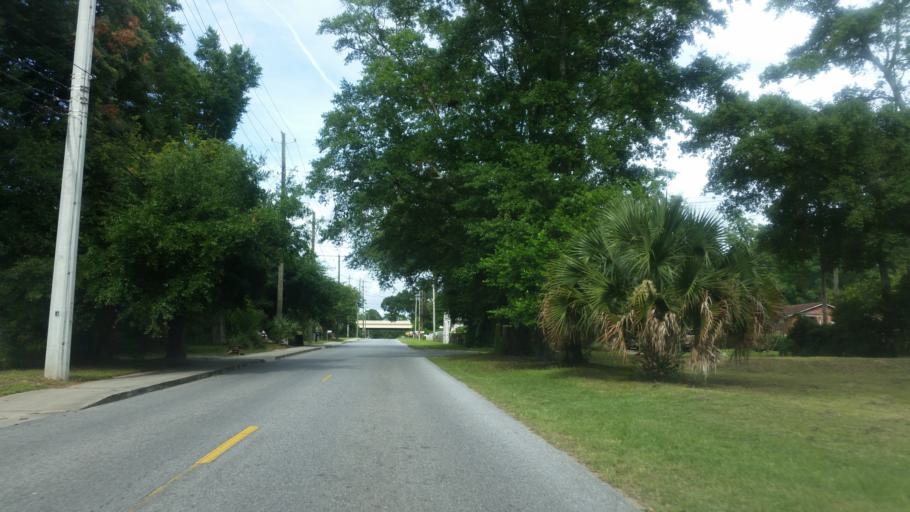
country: US
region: Florida
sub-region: Escambia County
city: Goulding
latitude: 30.4396
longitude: -87.2192
